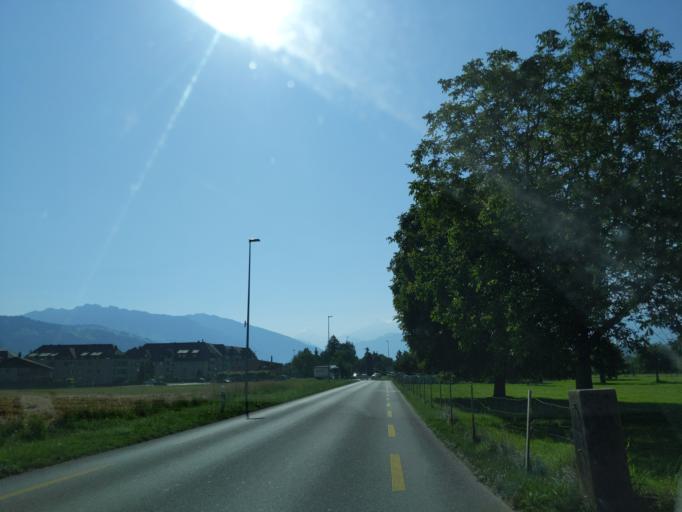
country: CH
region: Bern
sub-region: Thun District
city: Thun
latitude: 46.7334
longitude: 7.6096
